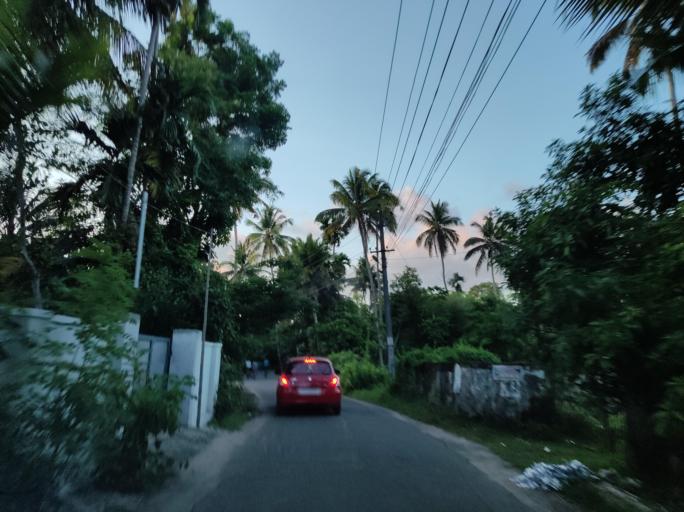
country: IN
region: Kerala
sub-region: Alappuzha
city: Vayalar
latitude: 9.7381
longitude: 76.2889
